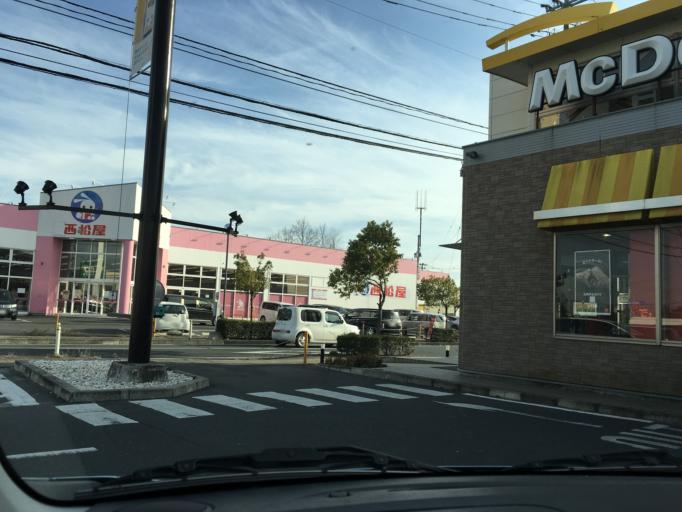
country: JP
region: Miyagi
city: Wakuya
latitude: 38.6859
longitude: 141.1863
